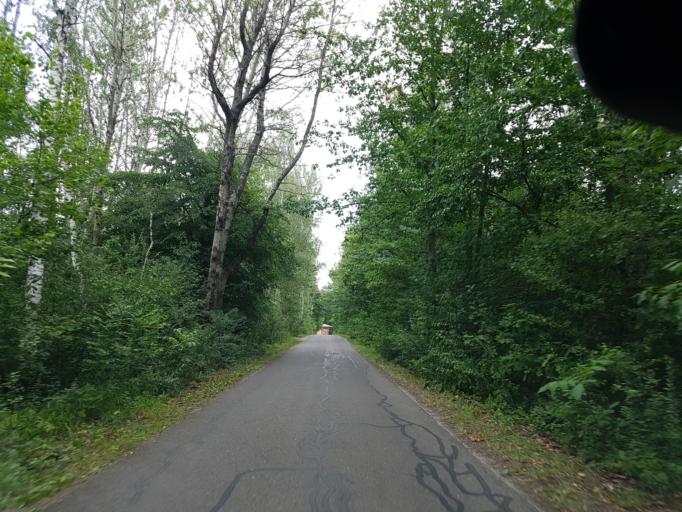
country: DE
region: Brandenburg
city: Sallgast
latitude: 51.5680
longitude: 13.8642
